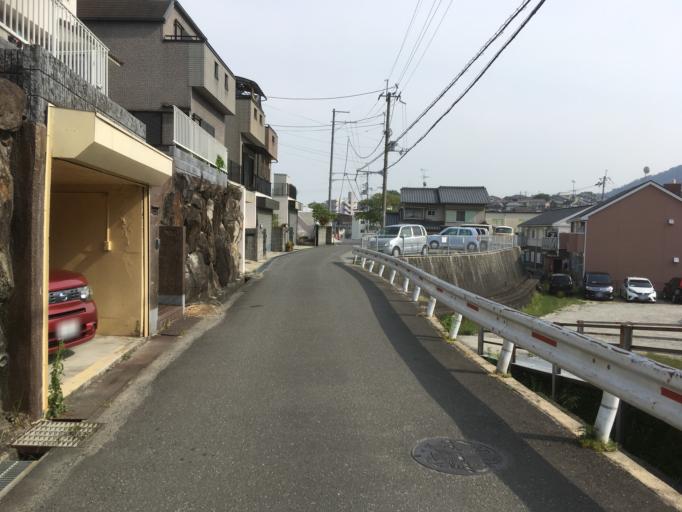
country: JP
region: Nara
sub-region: Ikoma-shi
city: Ikoma
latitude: 34.7014
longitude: 135.6978
